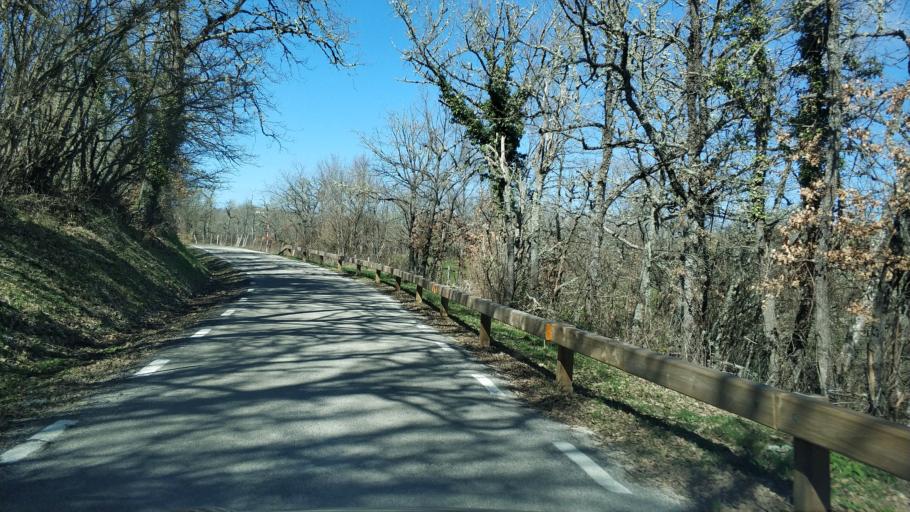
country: ES
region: Cantabria
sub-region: Provincia de Cantabria
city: Mataporquera
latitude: 42.8705
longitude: -4.0794
